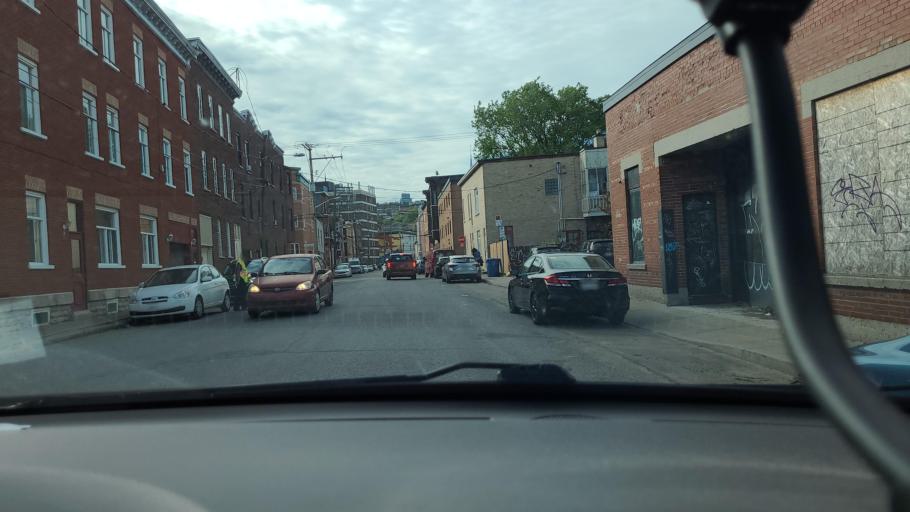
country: CA
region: Quebec
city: Quebec
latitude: 46.8150
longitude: -71.2306
